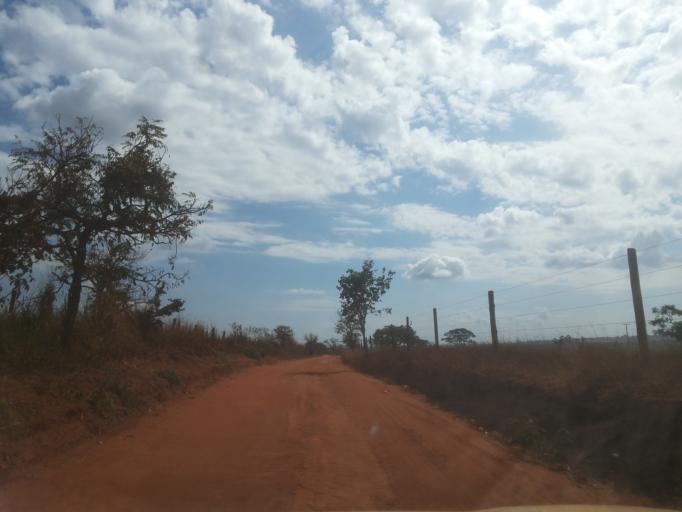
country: BR
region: Minas Gerais
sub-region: Ituiutaba
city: Ituiutaba
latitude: -19.0229
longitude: -49.3946
